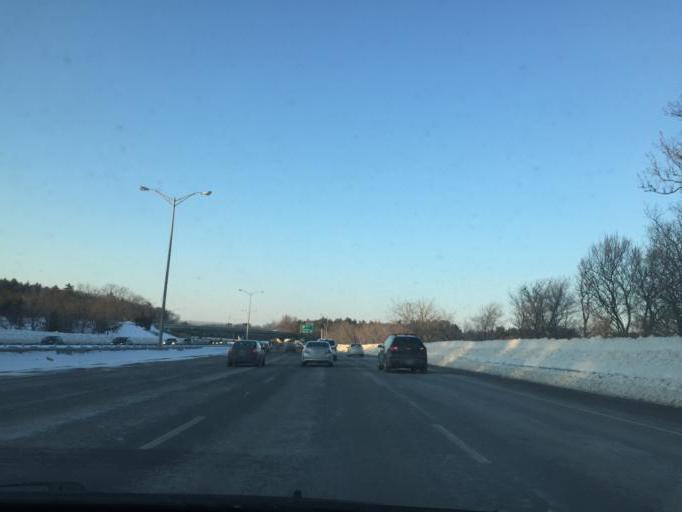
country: US
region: Massachusetts
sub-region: Middlesex County
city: Stoneham
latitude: 42.4563
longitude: -71.1022
